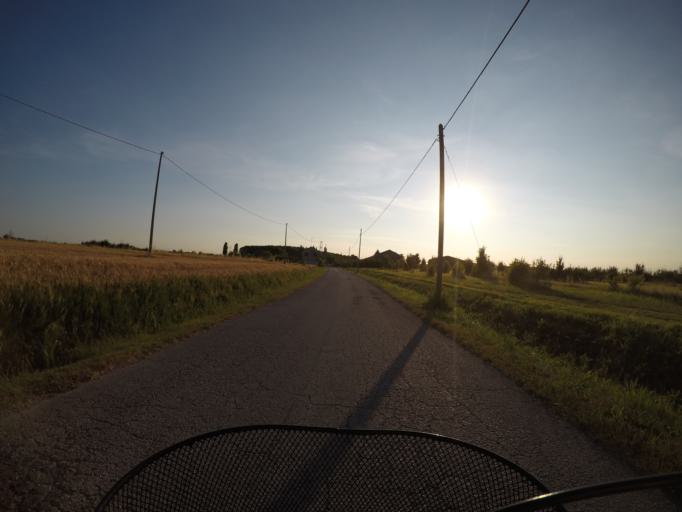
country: IT
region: Veneto
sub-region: Provincia di Rovigo
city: San Bellino
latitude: 45.0196
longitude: 11.5884
